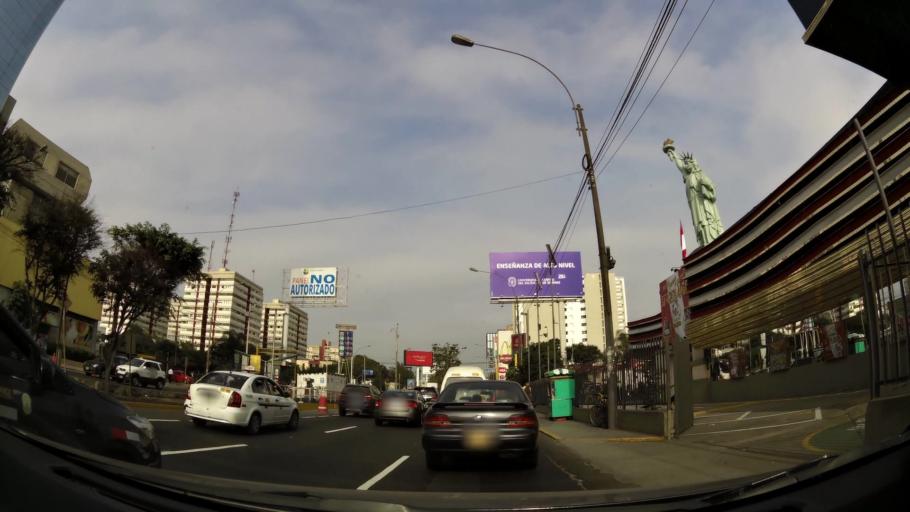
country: PE
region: Lima
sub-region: Lima
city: San Isidro
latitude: -12.0898
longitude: -77.0583
